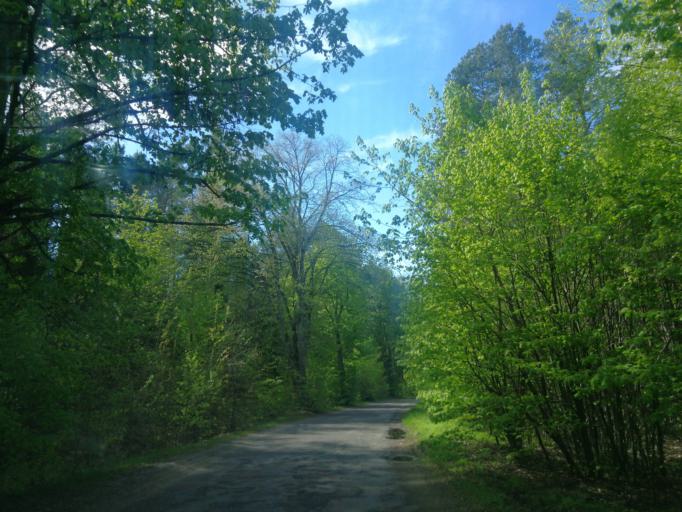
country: PL
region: Warmian-Masurian Voivodeship
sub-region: Powiat ilawski
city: Zalewo
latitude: 53.7078
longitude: 19.6840
